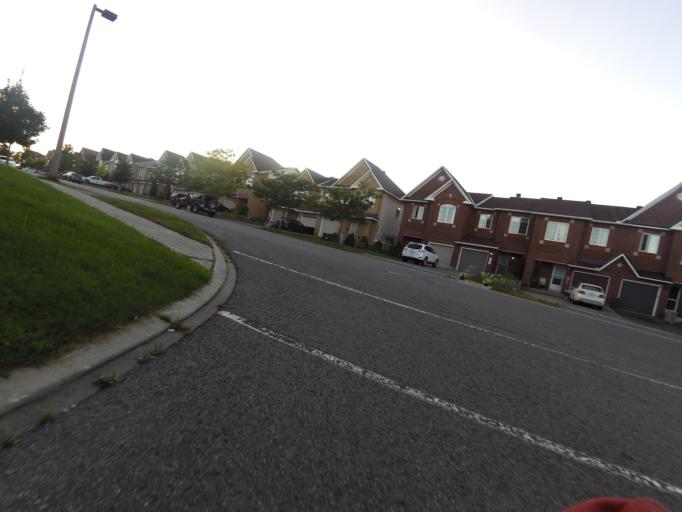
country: CA
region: Ontario
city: Bells Corners
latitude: 45.3492
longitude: -75.9415
